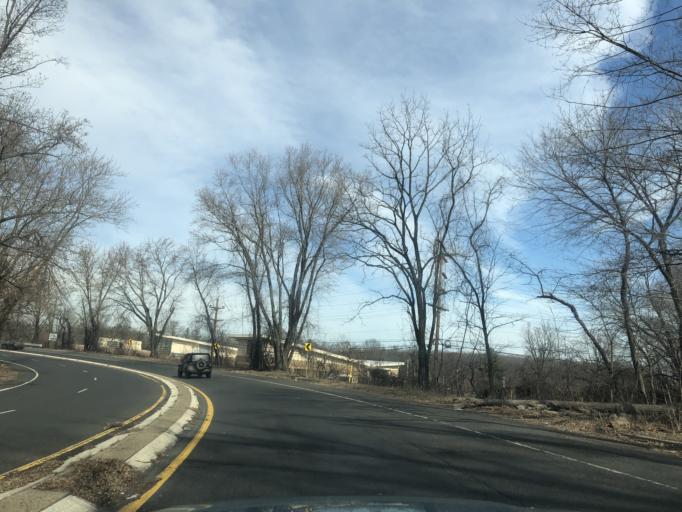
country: US
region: Pennsylvania
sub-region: Bucks County
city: Langhorne Manor
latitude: 40.1681
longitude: -74.9142
